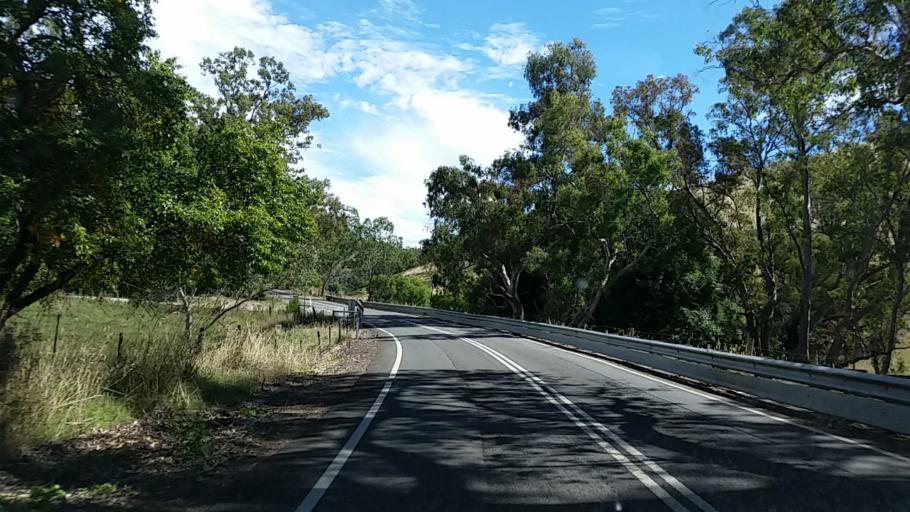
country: AU
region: South Australia
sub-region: Adelaide Hills
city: Gumeracha
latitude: -34.8308
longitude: 138.8497
